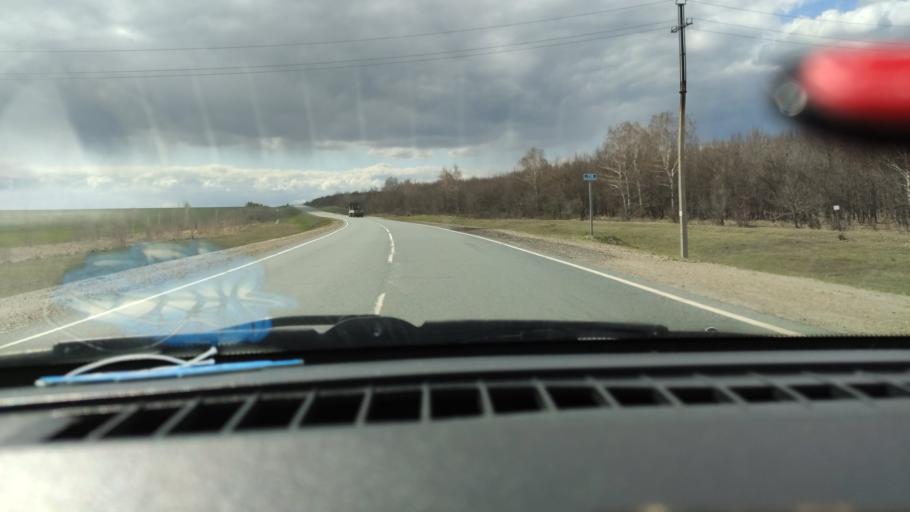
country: RU
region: Saratov
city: Alekseyevka
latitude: 52.2390
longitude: 47.9056
